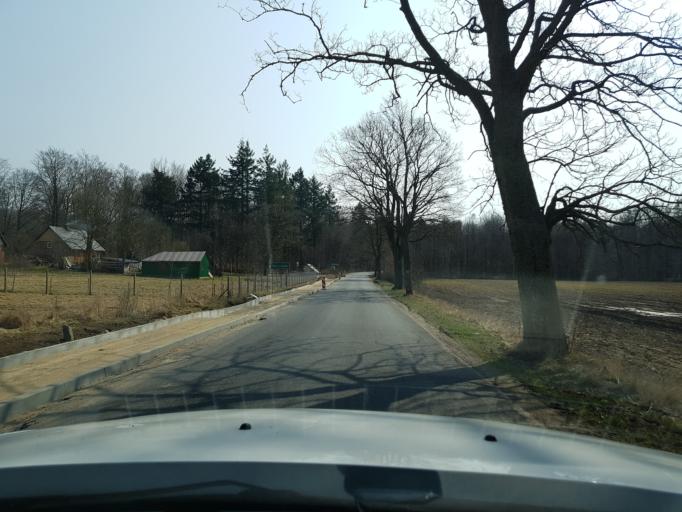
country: PL
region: West Pomeranian Voivodeship
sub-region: Powiat koszalinski
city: Sianow
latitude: 54.2737
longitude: 16.3140
